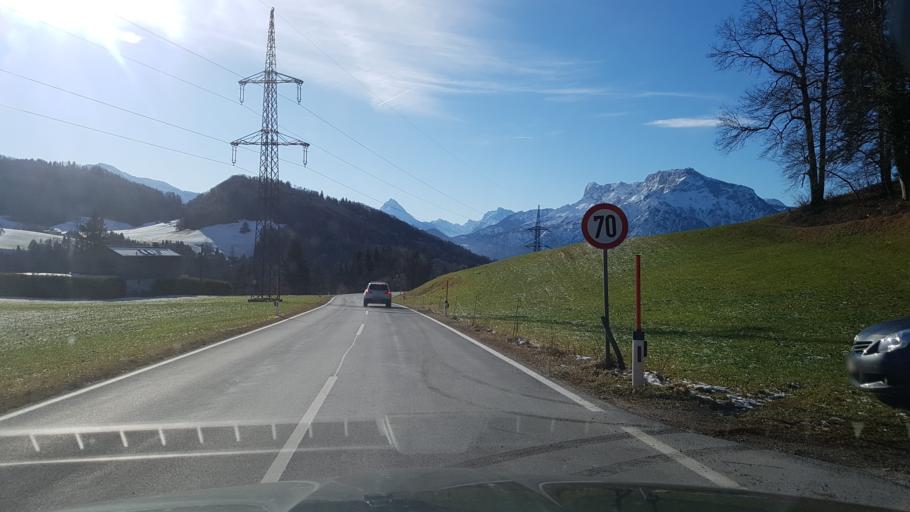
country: AT
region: Salzburg
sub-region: Politischer Bezirk Salzburg-Umgebung
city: Elsbethen
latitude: 47.7724
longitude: 13.1075
